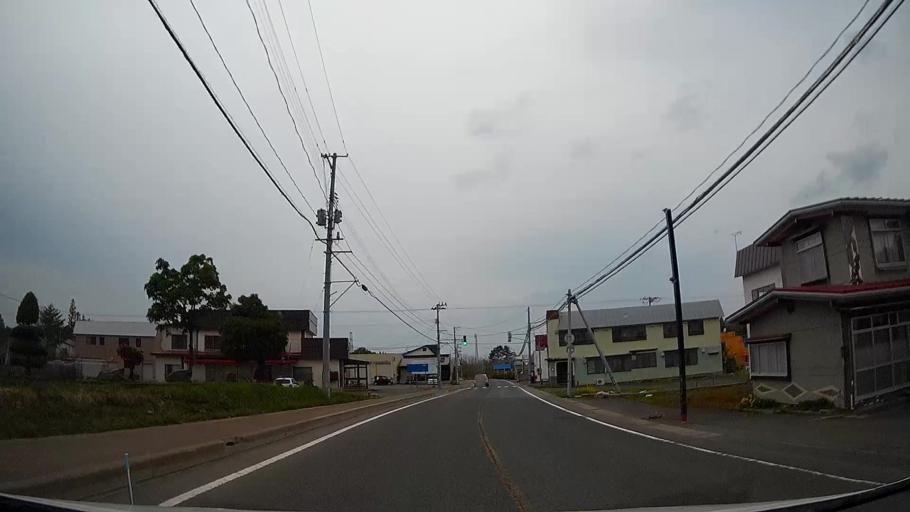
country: JP
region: Aomori
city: Aomori Shi
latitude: 40.7466
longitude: 140.7824
